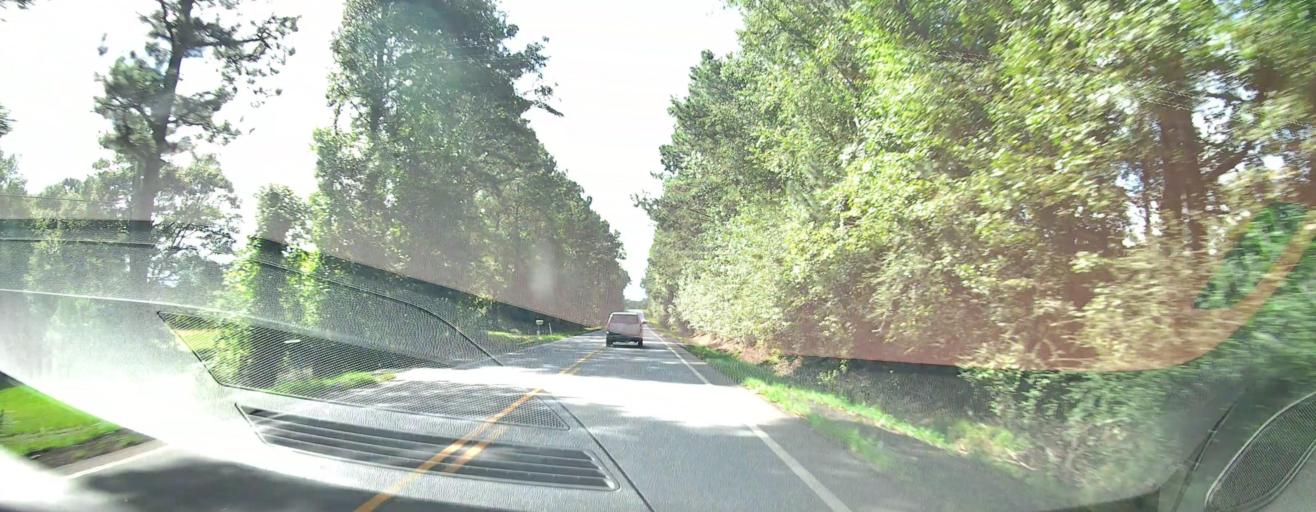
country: US
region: Georgia
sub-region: Upson County
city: Hannahs Mill
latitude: 32.9653
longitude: -84.4741
